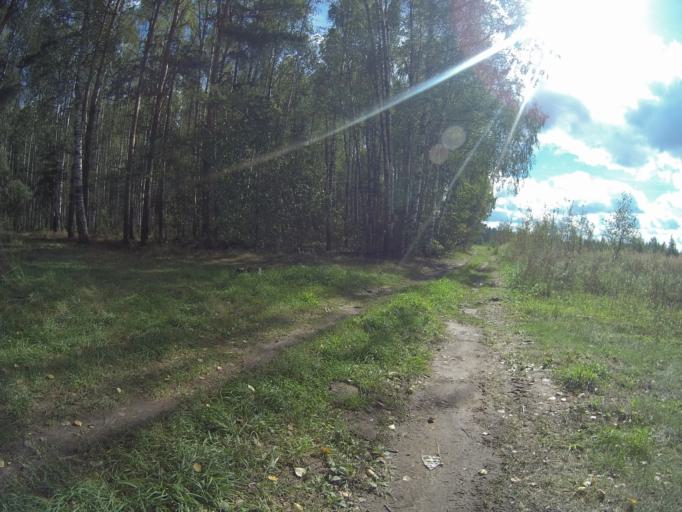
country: RU
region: Vladimir
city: Sudogda
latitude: 56.0659
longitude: 40.8033
